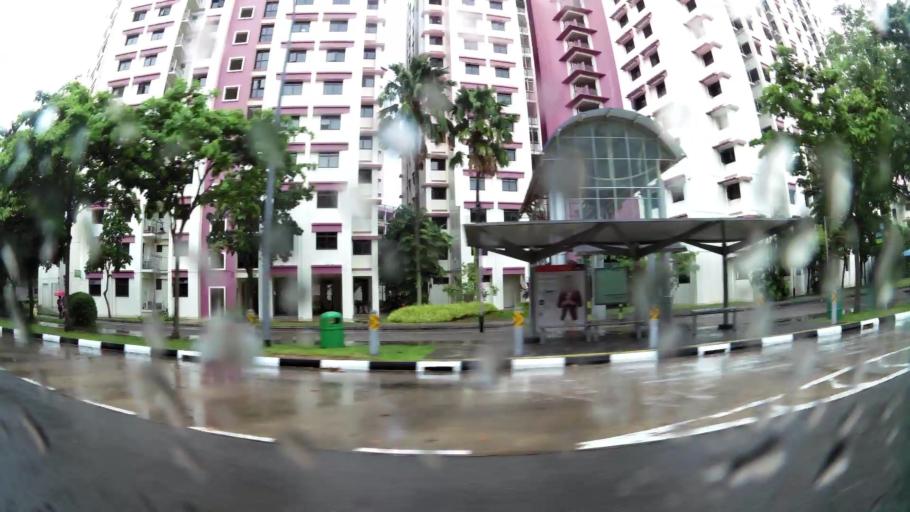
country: MY
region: Johor
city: Kampung Pasir Gudang Baru
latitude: 1.3867
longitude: 103.8925
